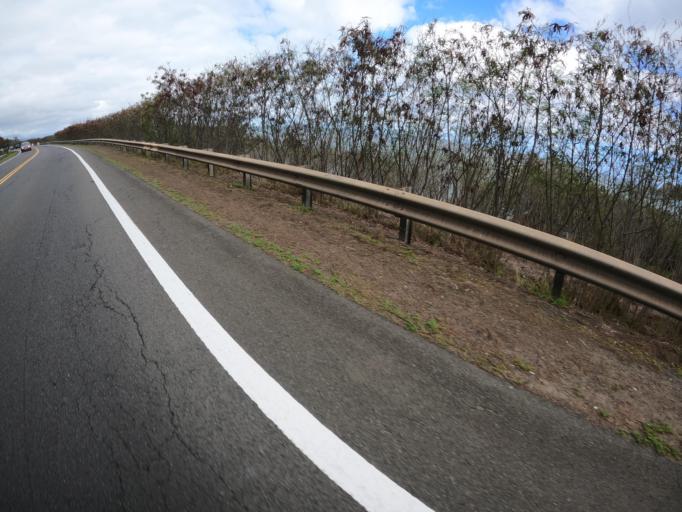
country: US
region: Hawaii
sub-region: Honolulu County
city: Waimanalo Beach
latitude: 21.3211
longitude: -157.6732
